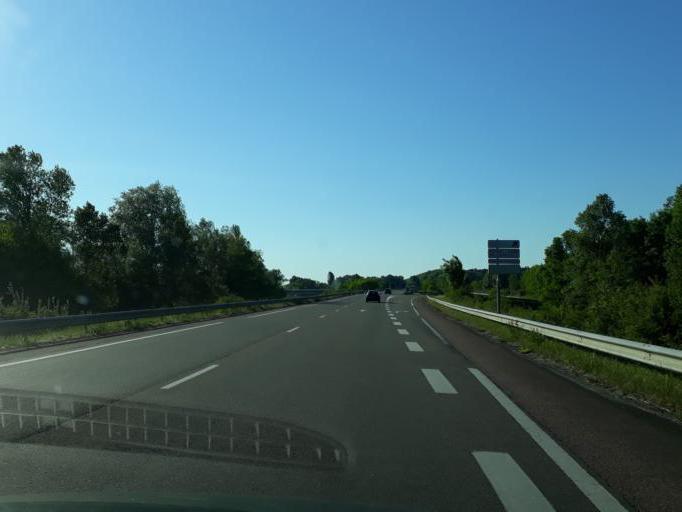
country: FR
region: Bourgogne
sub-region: Departement de la Nievre
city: Neuvy-sur-Loire
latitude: 47.5165
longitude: 2.8838
